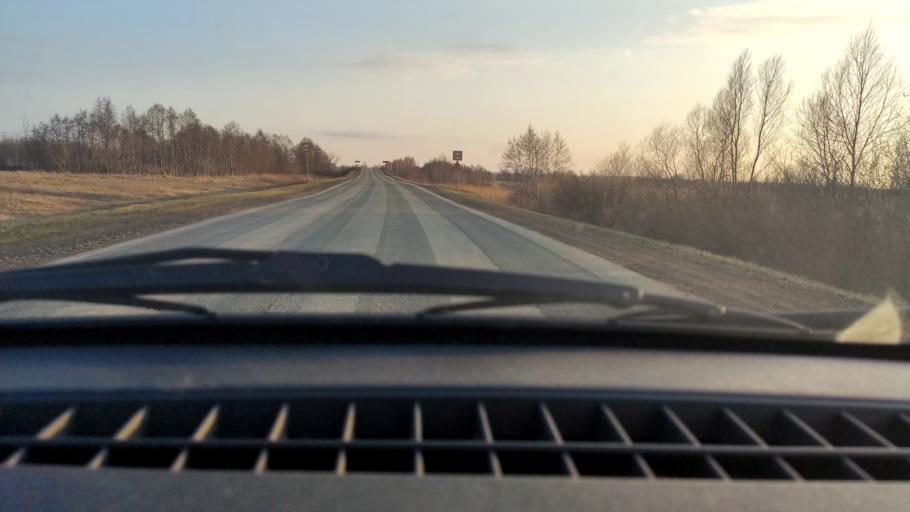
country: RU
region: Bashkortostan
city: Chishmy
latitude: 54.4439
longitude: 55.2420
